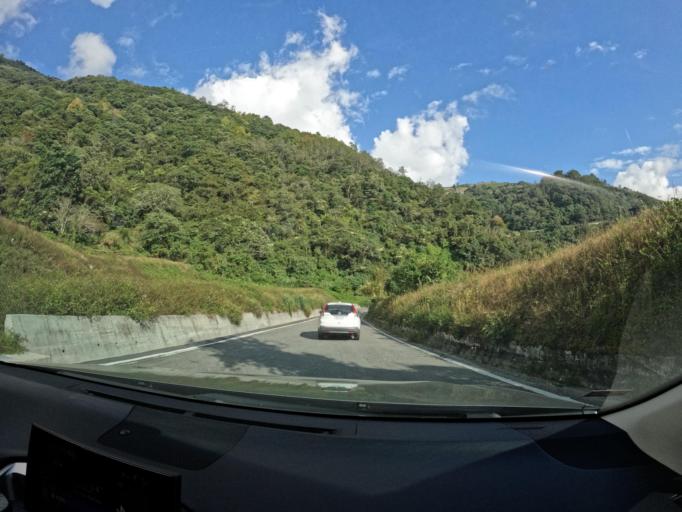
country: TW
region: Taiwan
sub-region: Taitung
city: Taitung
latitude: 23.2017
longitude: 121.0178
